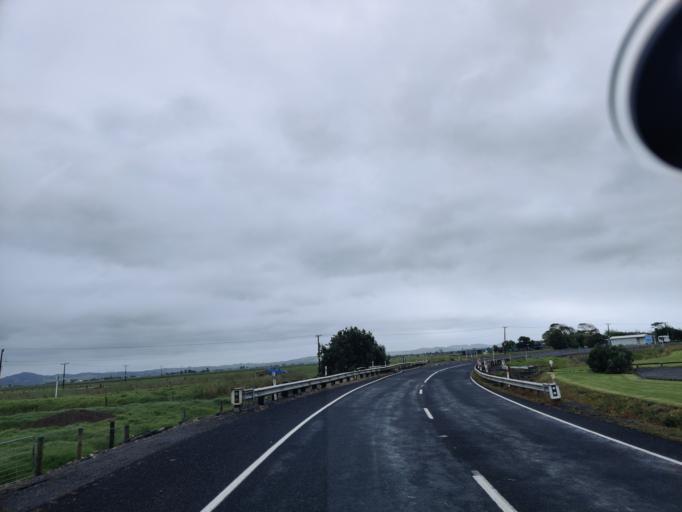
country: NZ
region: Northland
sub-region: Kaipara District
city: Dargaville
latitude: -36.1223
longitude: 174.0140
